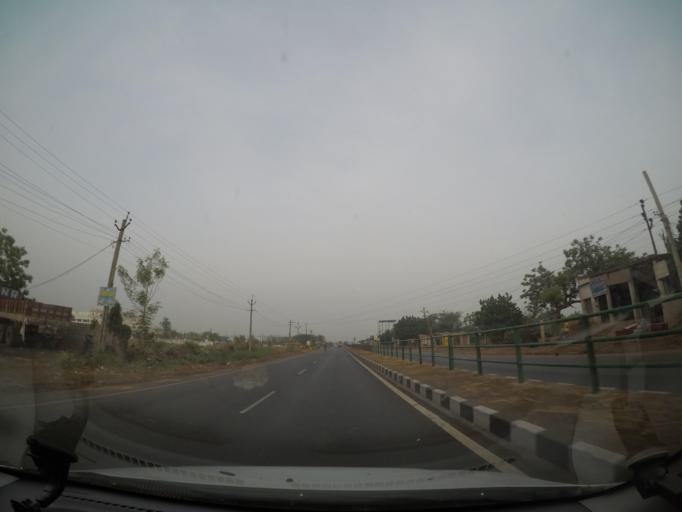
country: IN
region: Andhra Pradesh
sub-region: West Godavari
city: Eluru
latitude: 16.6329
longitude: 80.9578
